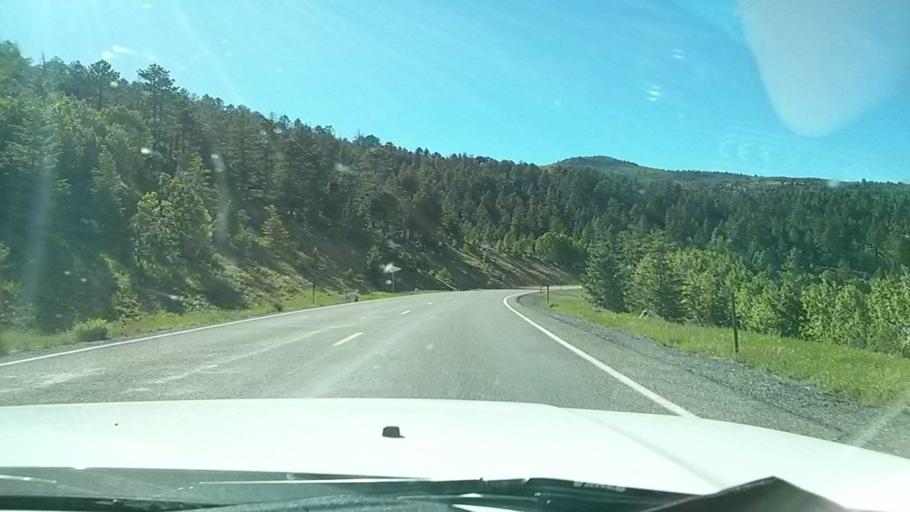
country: US
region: Utah
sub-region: Wayne County
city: Loa
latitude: 38.1205
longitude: -111.3270
